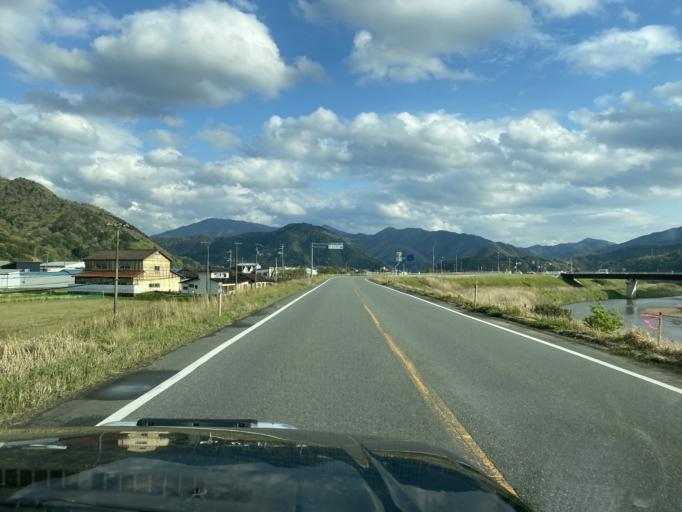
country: JP
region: Hyogo
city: Toyooka
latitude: 35.4829
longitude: 134.8615
